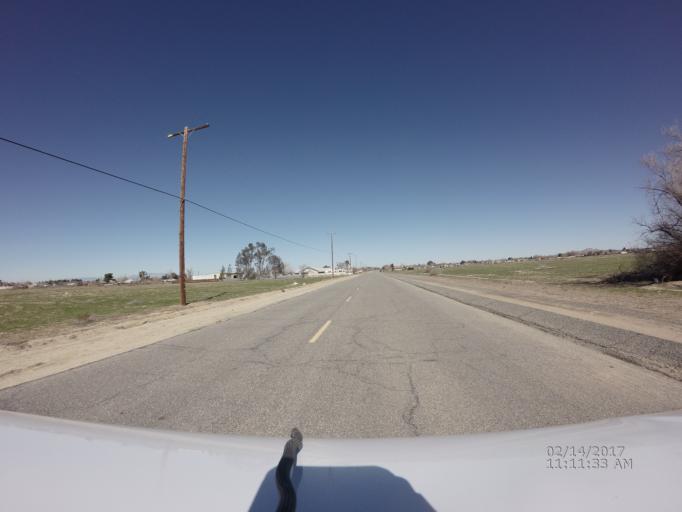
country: US
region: California
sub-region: Los Angeles County
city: Littlerock
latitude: 34.5666
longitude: -117.9608
